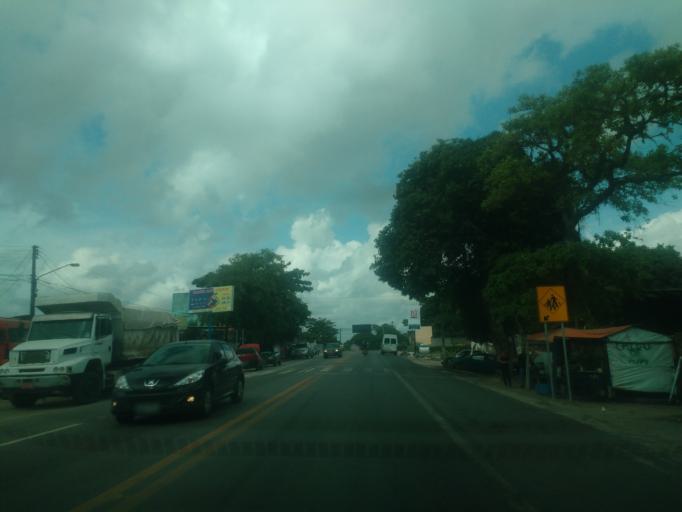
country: BR
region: Alagoas
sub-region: Satuba
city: Satuba
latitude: -9.5656
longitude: -35.7907
